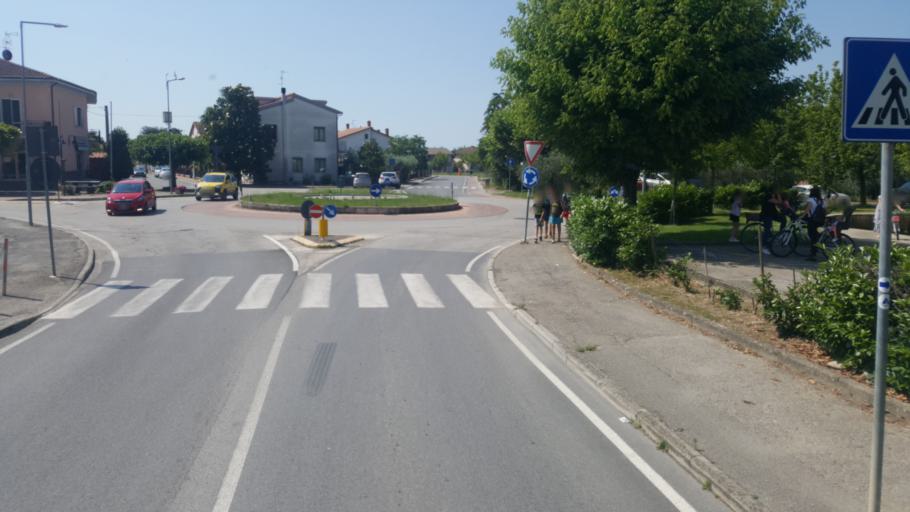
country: IT
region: Umbria
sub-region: Provincia di Perugia
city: Castiglione del Lago
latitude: 43.1262
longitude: 12.0422
